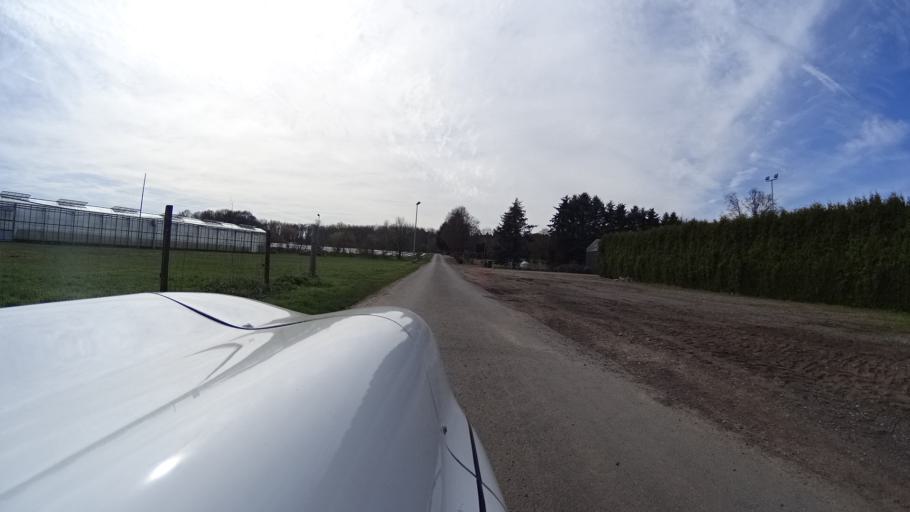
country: DE
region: North Rhine-Westphalia
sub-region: Regierungsbezirk Dusseldorf
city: Kevelaer
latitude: 51.5647
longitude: 6.1987
